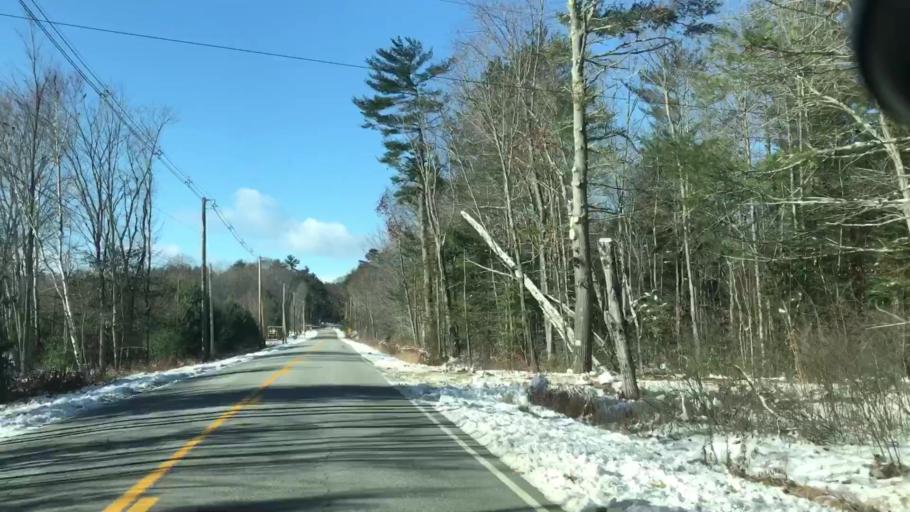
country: US
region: Maine
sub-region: Oxford County
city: Brownfield
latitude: 43.9650
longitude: -70.8700
